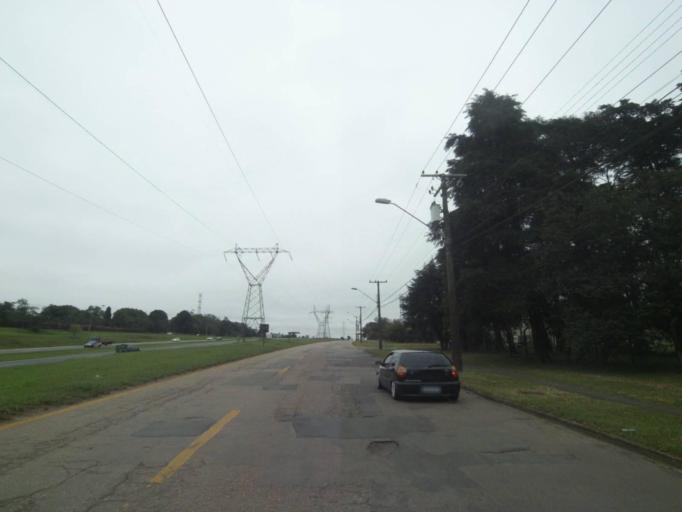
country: BR
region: Parana
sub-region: Araucaria
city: Araucaria
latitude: -25.5463
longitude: -49.3189
